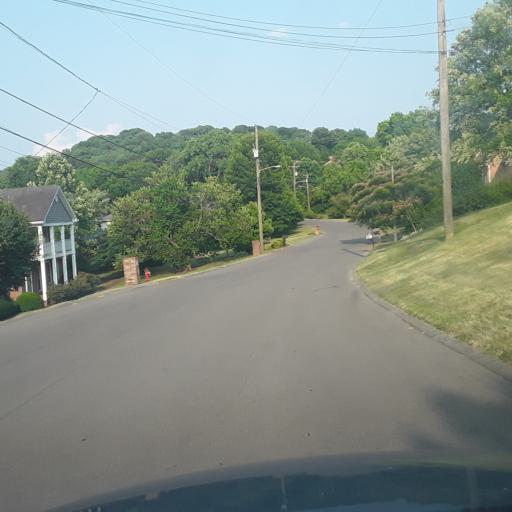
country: US
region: Tennessee
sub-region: Williamson County
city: Brentwood Estates
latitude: 36.0382
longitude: -86.7370
